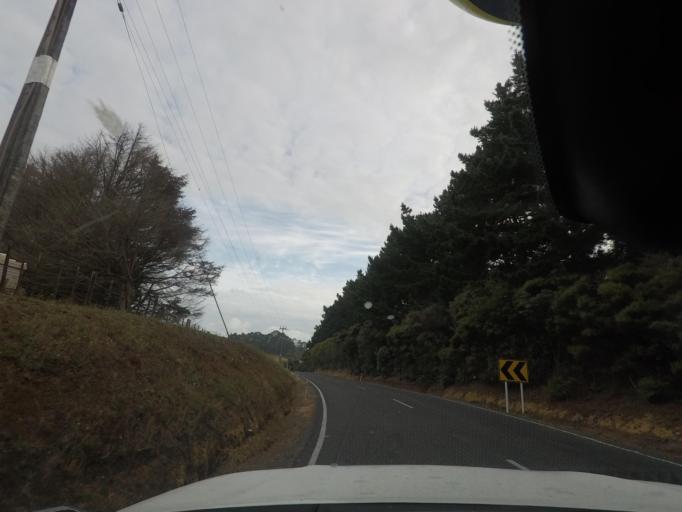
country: NZ
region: Auckland
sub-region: Auckland
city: Parakai
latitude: -36.5360
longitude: 174.2926
